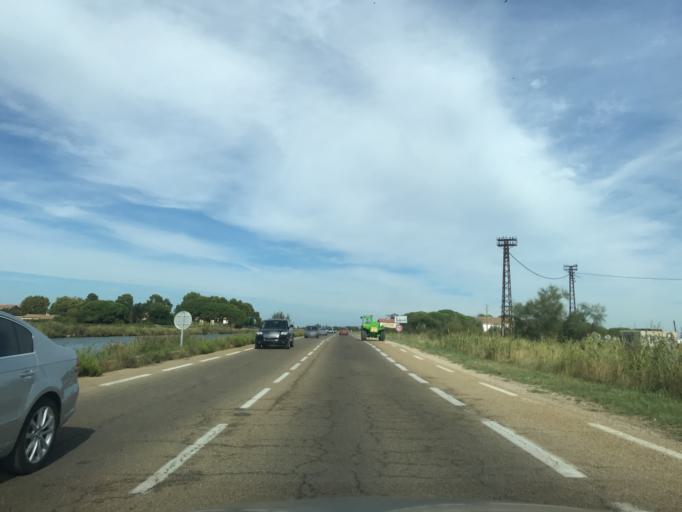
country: FR
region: Languedoc-Roussillon
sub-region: Departement du Gard
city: Le Grau-du-Roi
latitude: 43.5494
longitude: 4.1648
